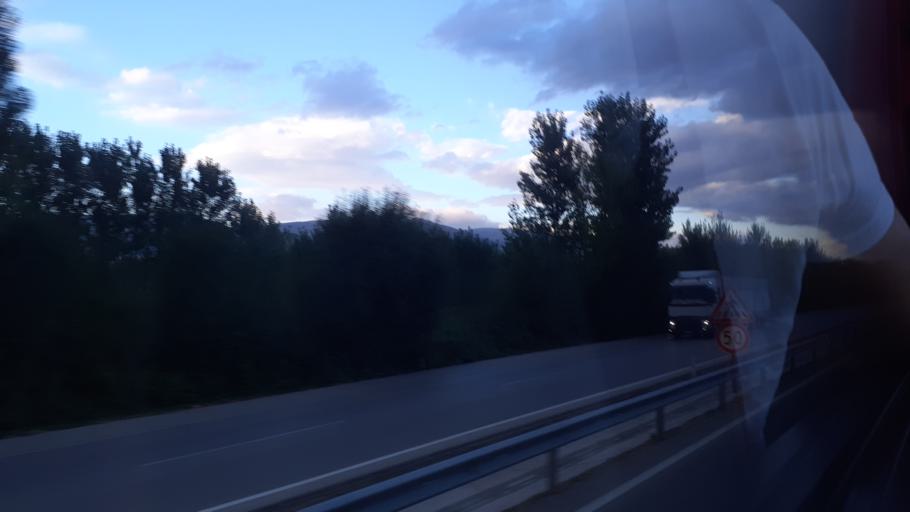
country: TR
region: Tokat
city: Dokmetepe
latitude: 40.3217
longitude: 36.2088
